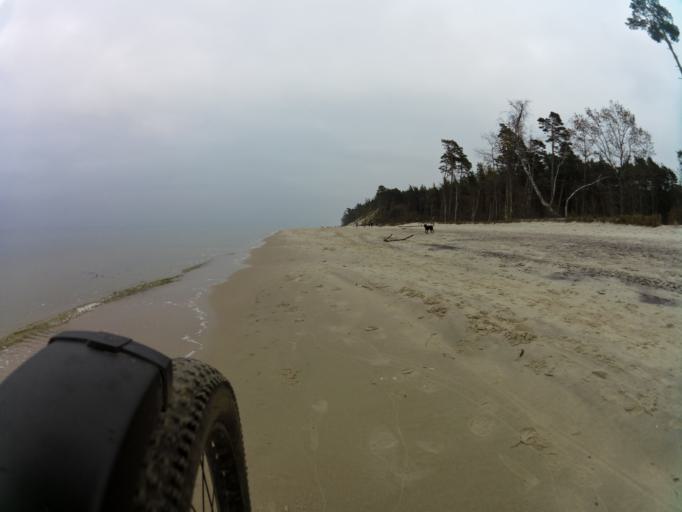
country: PL
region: Pomeranian Voivodeship
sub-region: Powiat pucki
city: Krokowa
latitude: 54.8319
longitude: 18.1391
